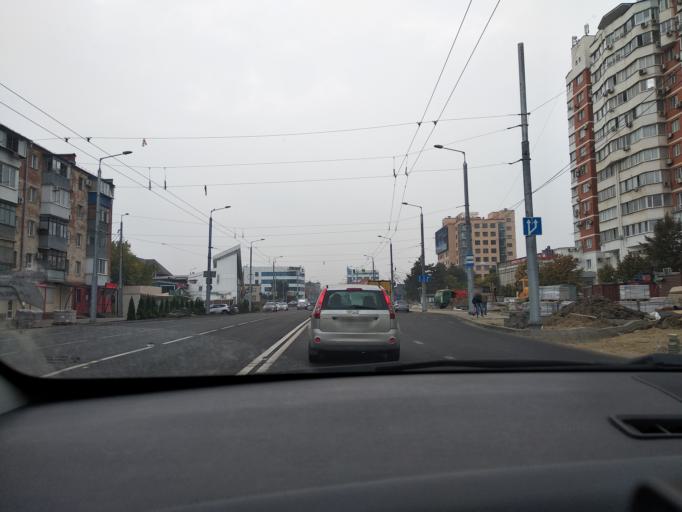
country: RU
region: Krasnodarskiy
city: Krasnodar
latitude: 45.0525
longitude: 38.9595
